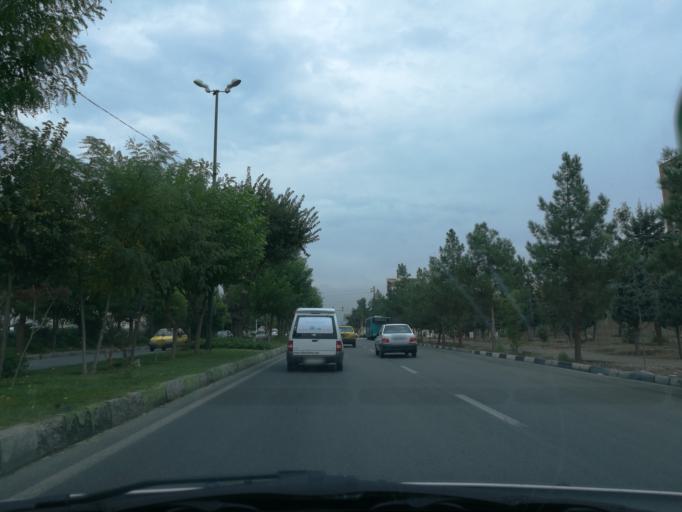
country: IR
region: Alborz
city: Karaj
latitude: 35.8594
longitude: 50.9439
